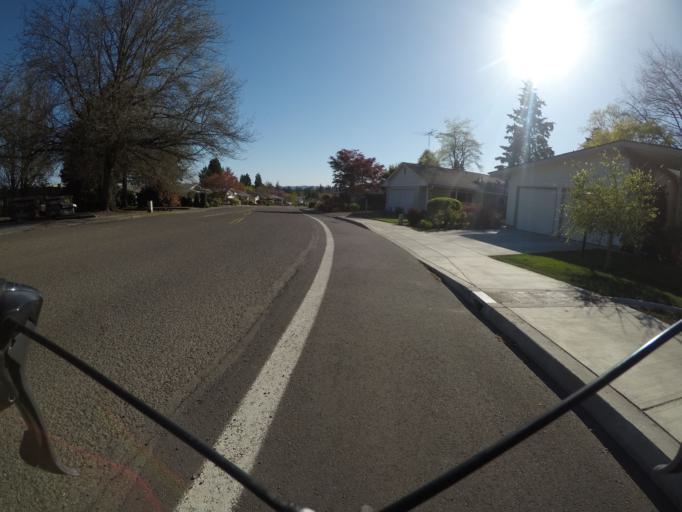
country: US
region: Oregon
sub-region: Washington County
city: King City
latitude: 45.4082
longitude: -122.7968
